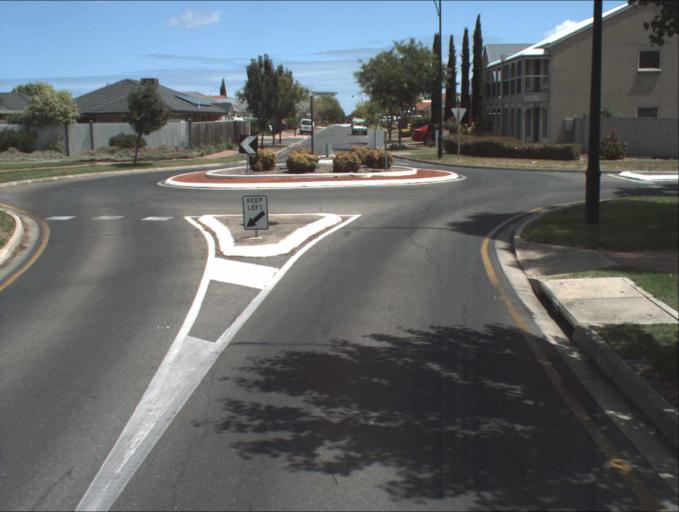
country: AU
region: South Australia
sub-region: Salisbury
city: Ingle Farm
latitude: -34.8490
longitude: 138.6331
